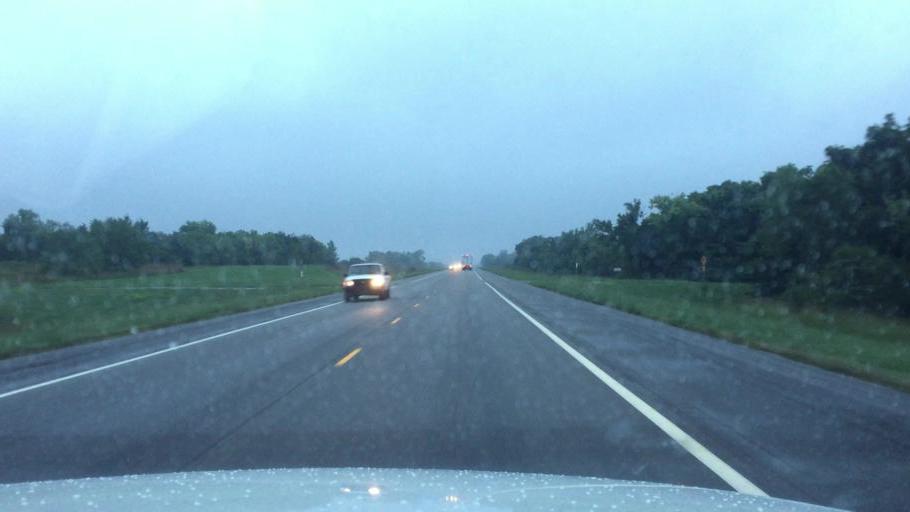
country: US
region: Kansas
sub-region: Montgomery County
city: Cherryvale
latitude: 37.4354
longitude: -95.4882
